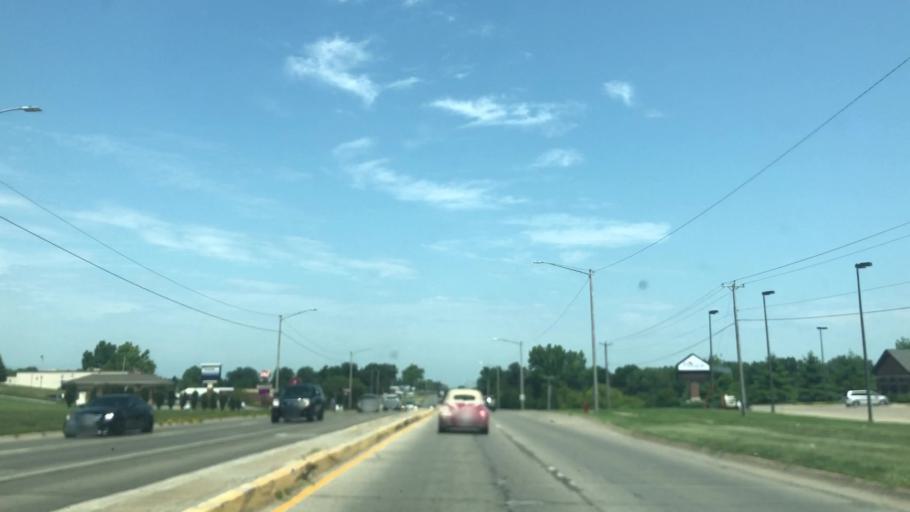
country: US
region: Iowa
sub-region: Marshall County
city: Marshalltown
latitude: 42.0183
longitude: -92.9123
